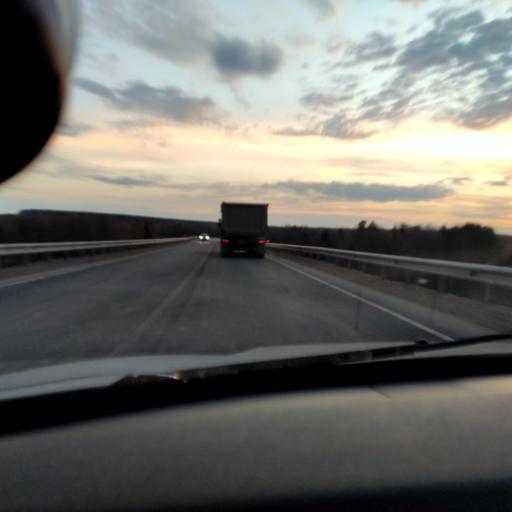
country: RU
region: Perm
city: Chusovoy
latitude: 58.3303
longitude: 57.7755
